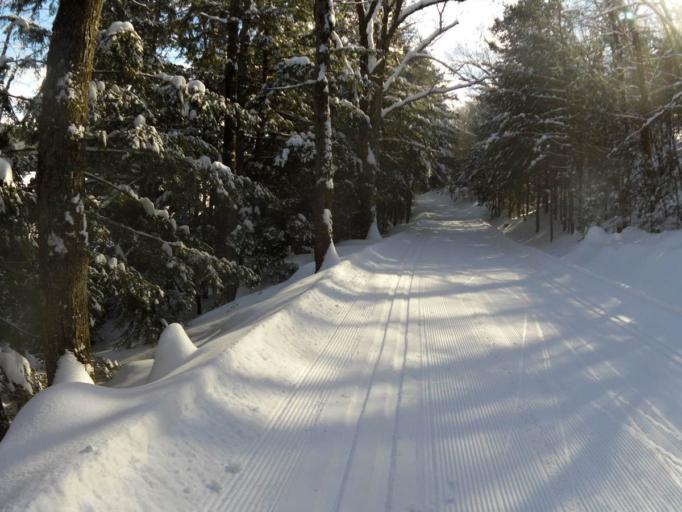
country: CA
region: Quebec
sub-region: Outaouais
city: Wakefield
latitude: 45.5949
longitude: -75.9913
